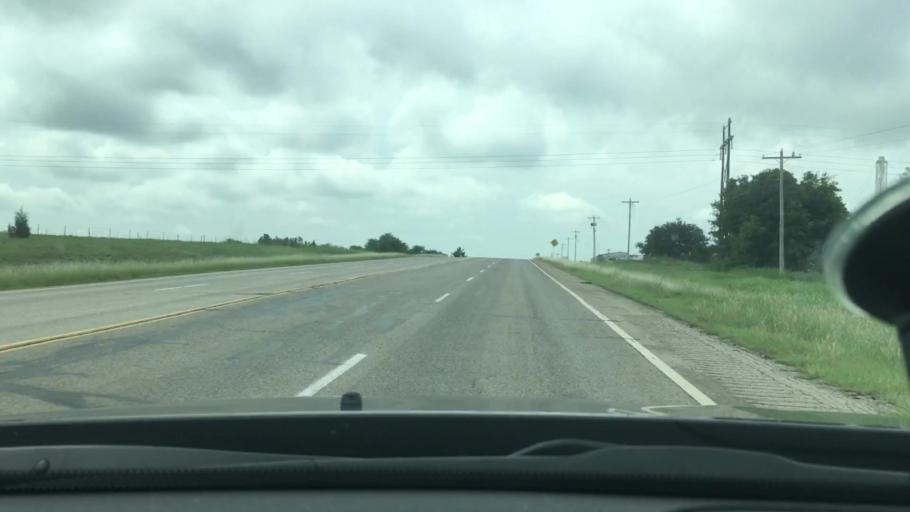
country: US
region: Oklahoma
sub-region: Carter County
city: Wilson
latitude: 34.1813
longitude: -97.4749
